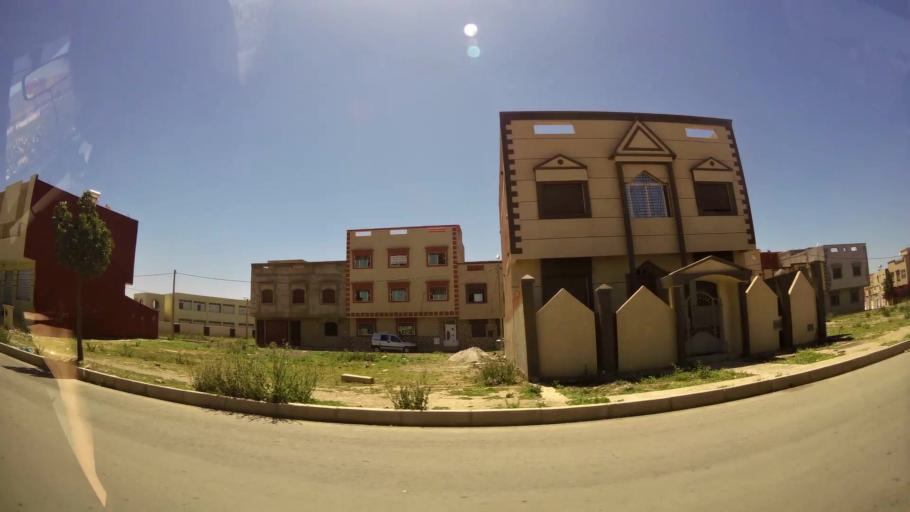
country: MA
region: Oriental
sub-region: Oujda-Angad
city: Oujda
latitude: 34.6743
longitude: -1.8664
